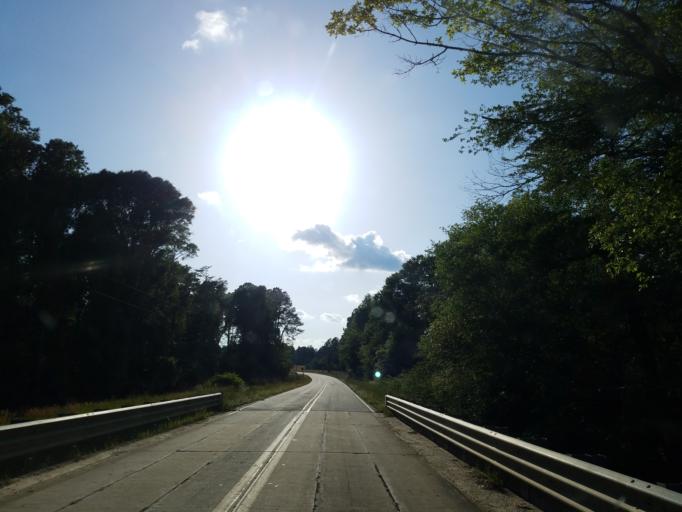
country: US
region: Georgia
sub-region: Turner County
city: Ashburn
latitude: 31.6096
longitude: -83.5727
